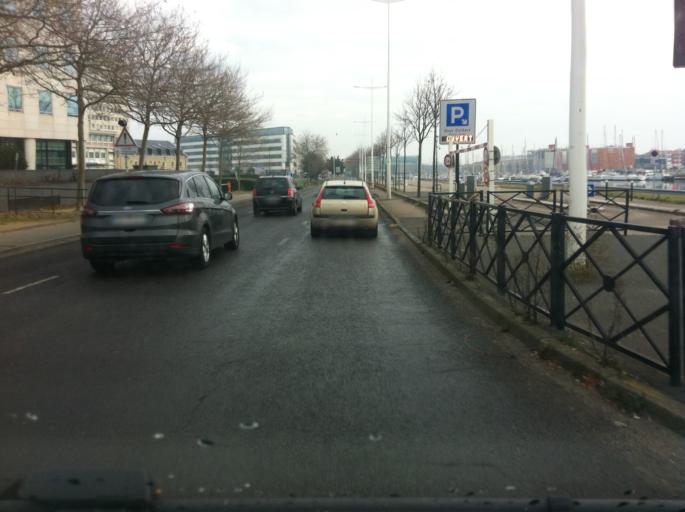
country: FR
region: Haute-Normandie
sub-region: Departement de la Seine-Maritime
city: Le Havre
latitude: 49.4899
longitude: 0.1196
